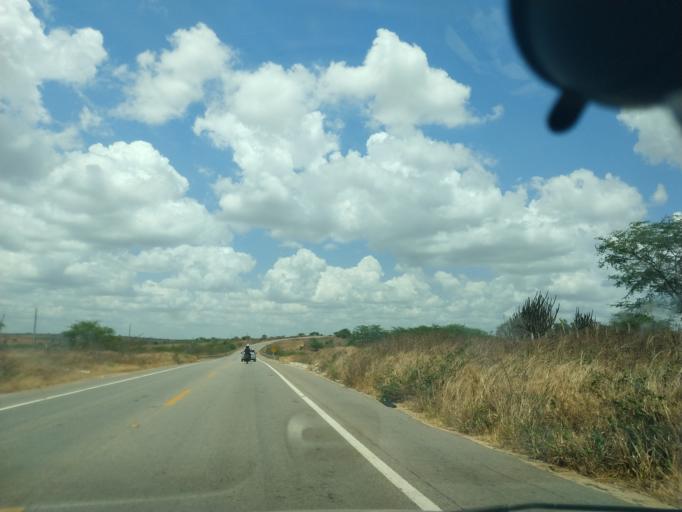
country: BR
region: Rio Grande do Norte
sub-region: Tangara
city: Tangara
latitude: -6.1858
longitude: -35.7776
